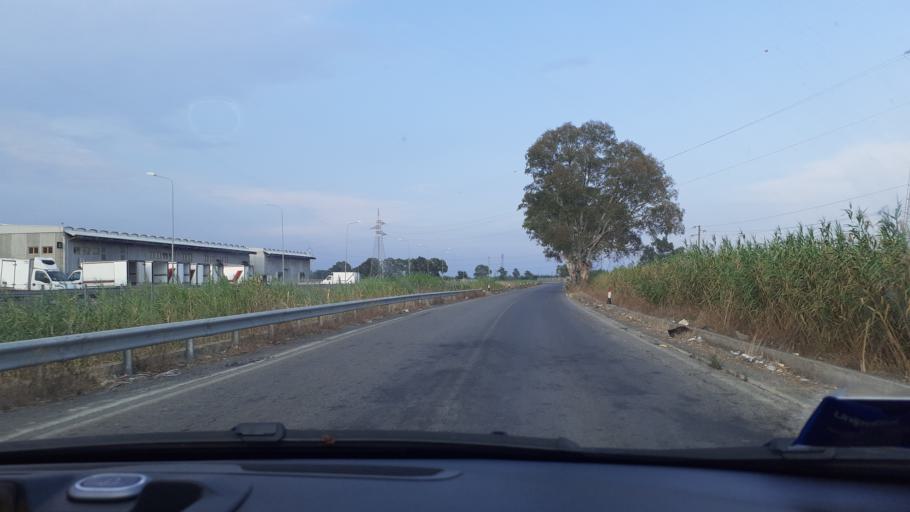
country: IT
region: Sicily
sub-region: Catania
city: Misterbianco
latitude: 37.4385
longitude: 15.0049
